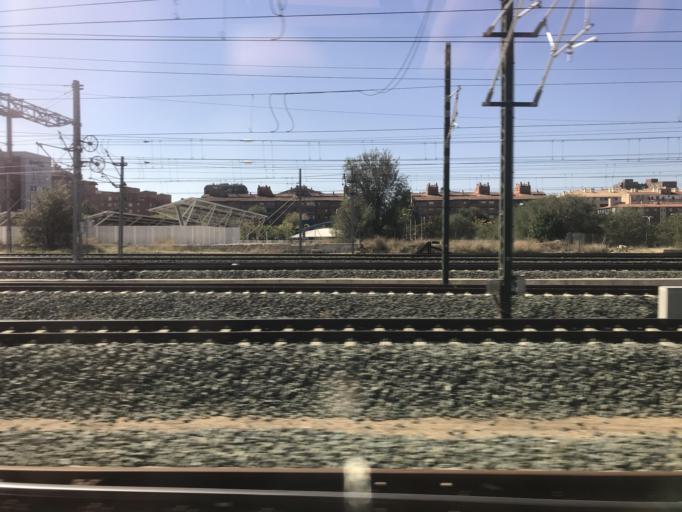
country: ES
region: Castille-La Mancha
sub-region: Provincia de Albacete
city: Albacete
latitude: 39.0016
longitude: -1.8485
